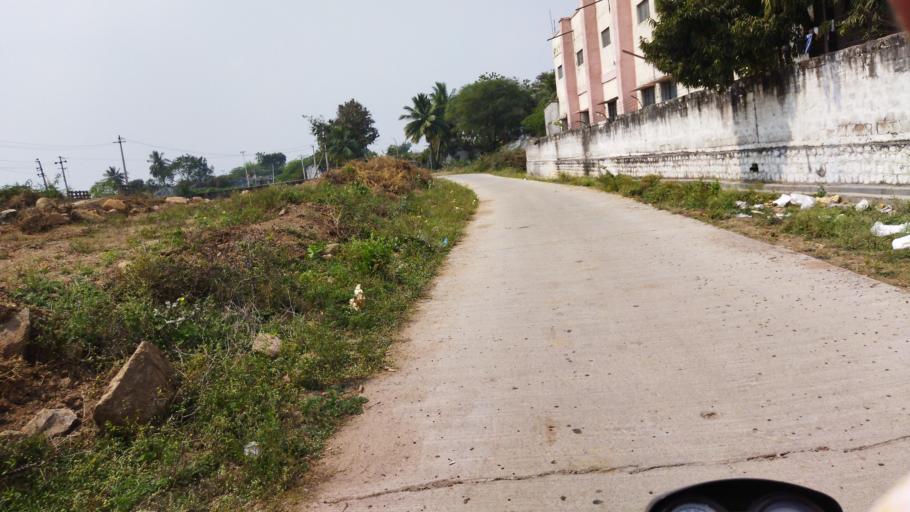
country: IN
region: Telangana
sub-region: Nalgonda
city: Nalgonda
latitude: 17.0845
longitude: 79.2750
